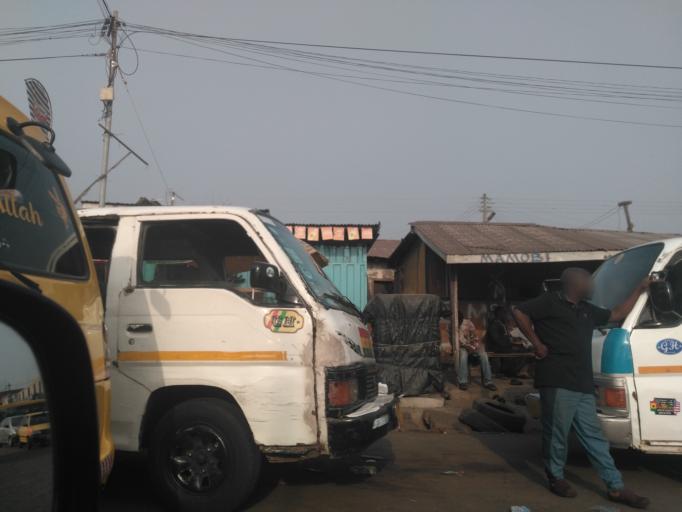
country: GH
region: Greater Accra
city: Accra
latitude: 5.5940
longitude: -0.1948
